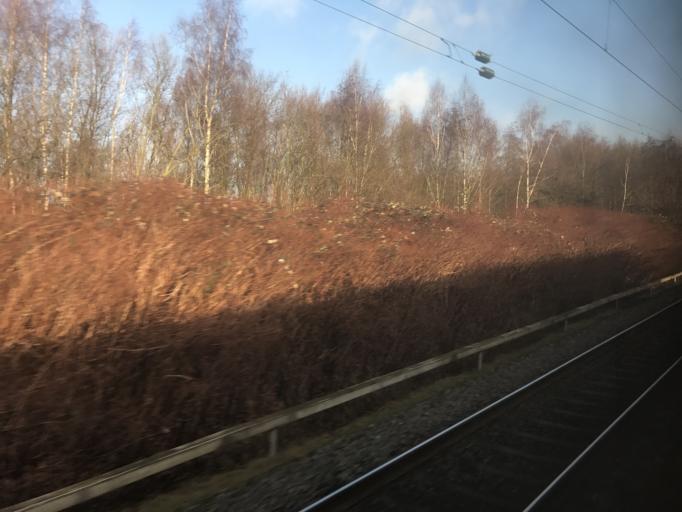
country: DE
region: North Rhine-Westphalia
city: Witten
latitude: 51.4938
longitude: 7.3576
